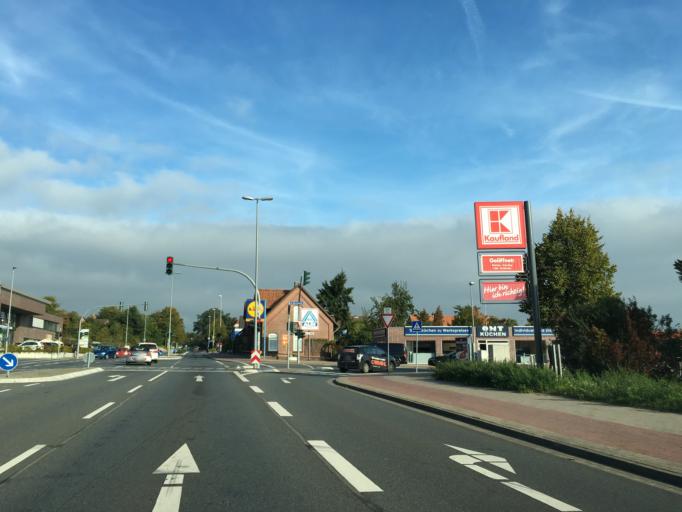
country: DE
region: Lower Saxony
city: Lueneburg
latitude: 53.2587
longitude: 10.4095
